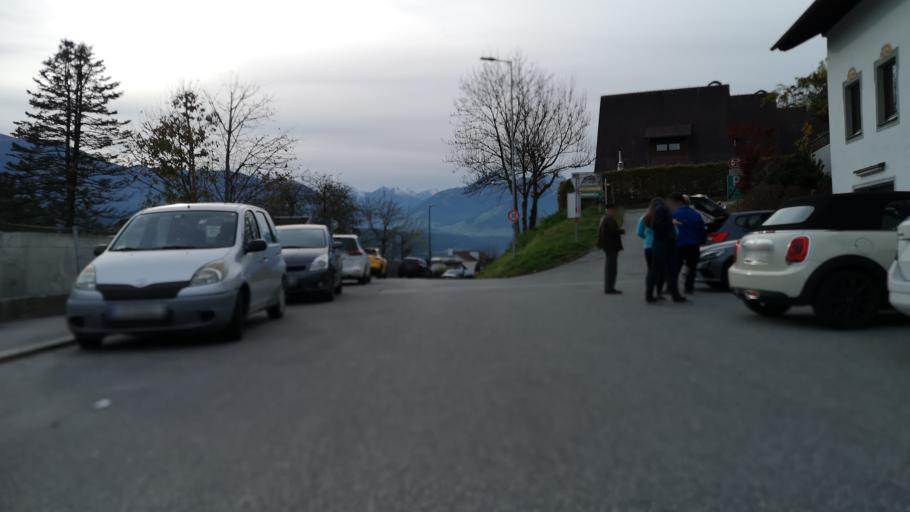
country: AT
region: Tyrol
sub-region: Politischer Bezirk Innsbruck Land
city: Vols
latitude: 47.2701
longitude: 11.3598
